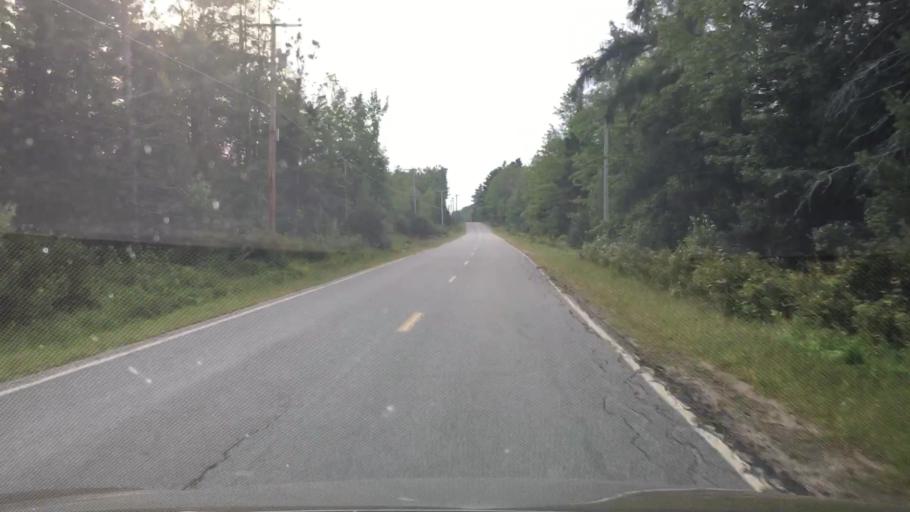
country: US
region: Maine
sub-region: Hancock County
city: Penobscot
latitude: 44.4713
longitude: -68.7509
